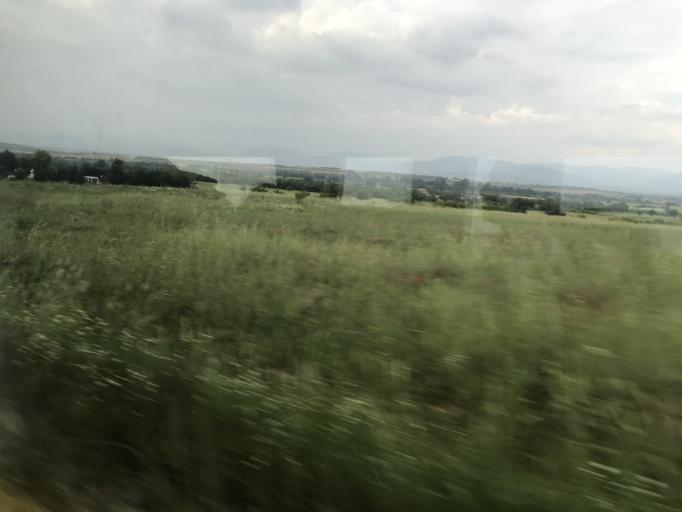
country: GR
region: East Macedonia and Thrace
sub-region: Nomos Rodopis
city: Sapes
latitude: 41.0316
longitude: 25.6805
